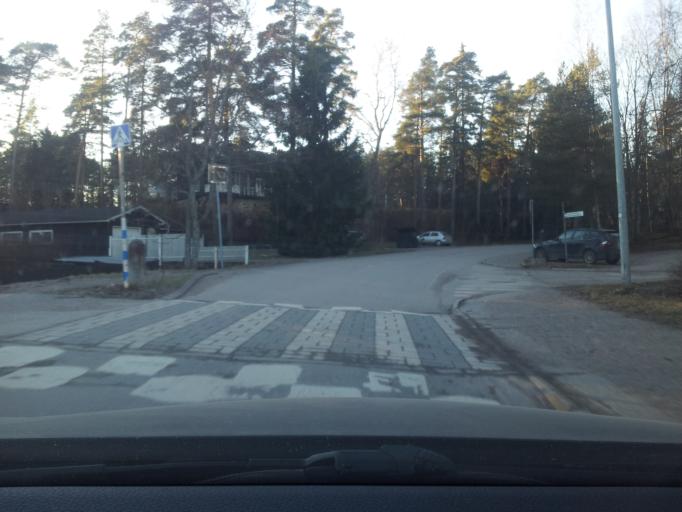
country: FI
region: Uusimaa
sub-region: Helsinki
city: Koukkuniemi
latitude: 60.1583
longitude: 24.7914
